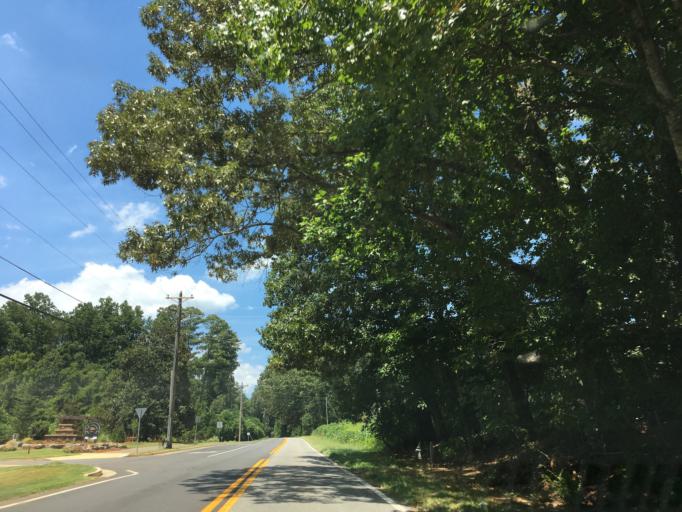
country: US
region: Georgia
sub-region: Fulton County
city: Milton
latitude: 34.1183
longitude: -84.3575
